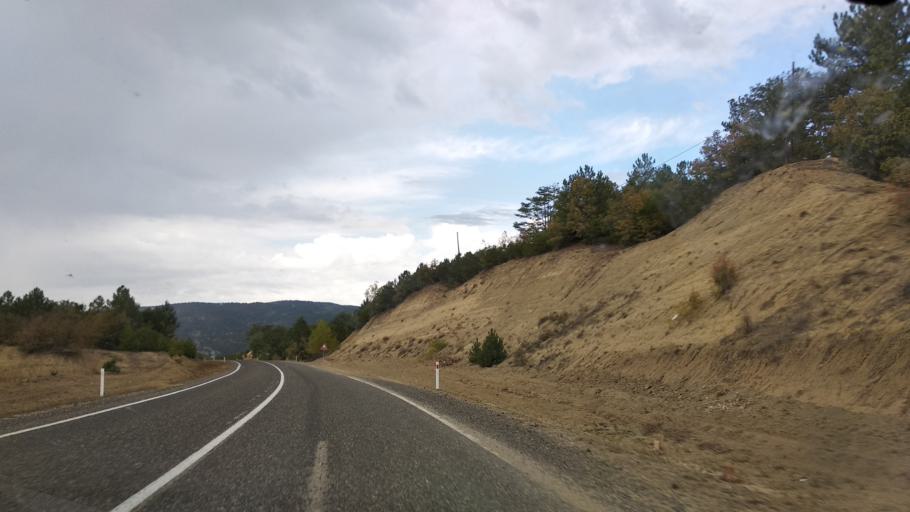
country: TR
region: Bolu
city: Seben
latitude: 40.3367
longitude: 31.4365
